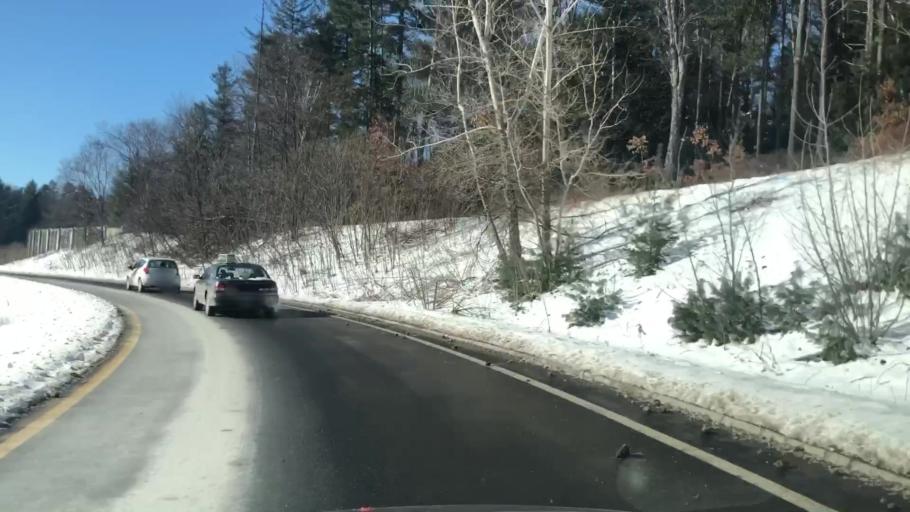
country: US
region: New Hampshire
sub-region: Hillsborough County
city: Bedford
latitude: 42.9573
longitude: -71.4847
